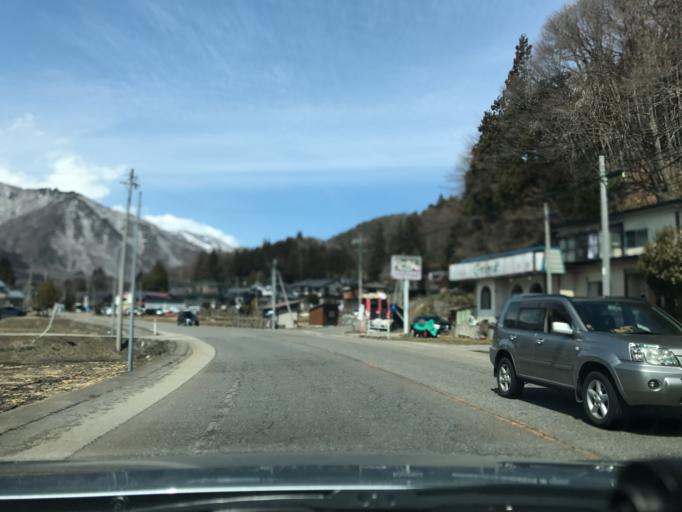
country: JP
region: Nagano
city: Omachi
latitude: 36.5640
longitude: 137.8435
